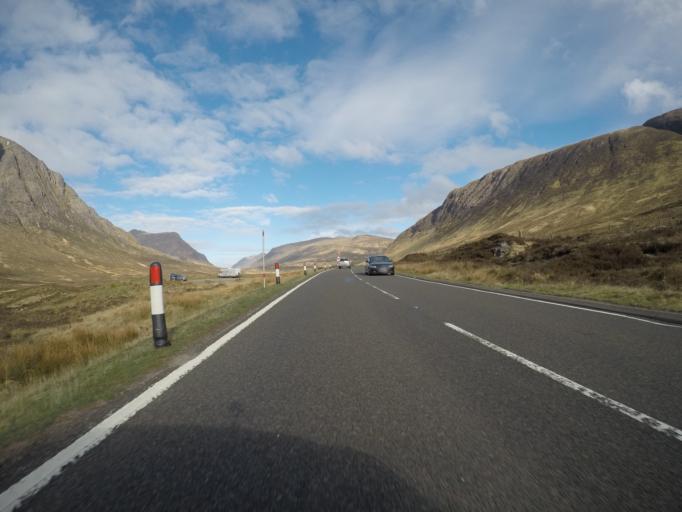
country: GB
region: Scotland
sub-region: Highland
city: Spean Bridge
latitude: 56.6568
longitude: -4.8770
